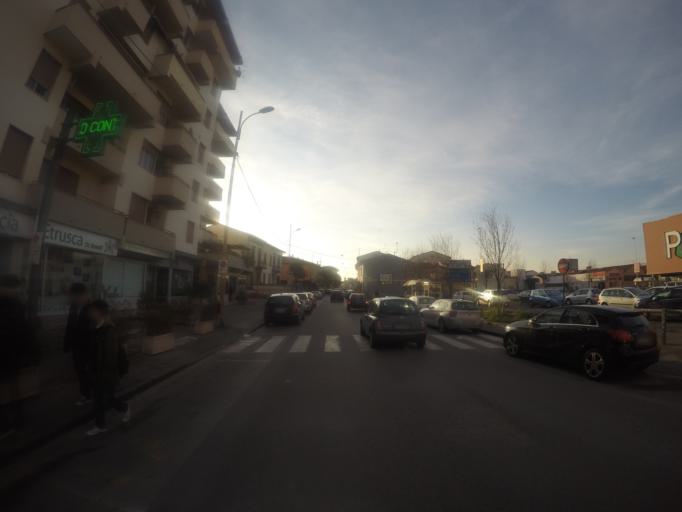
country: IT
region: Tuscany
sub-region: Provincia di Prato
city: Prato
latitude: 43.8865
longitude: 11.0843
